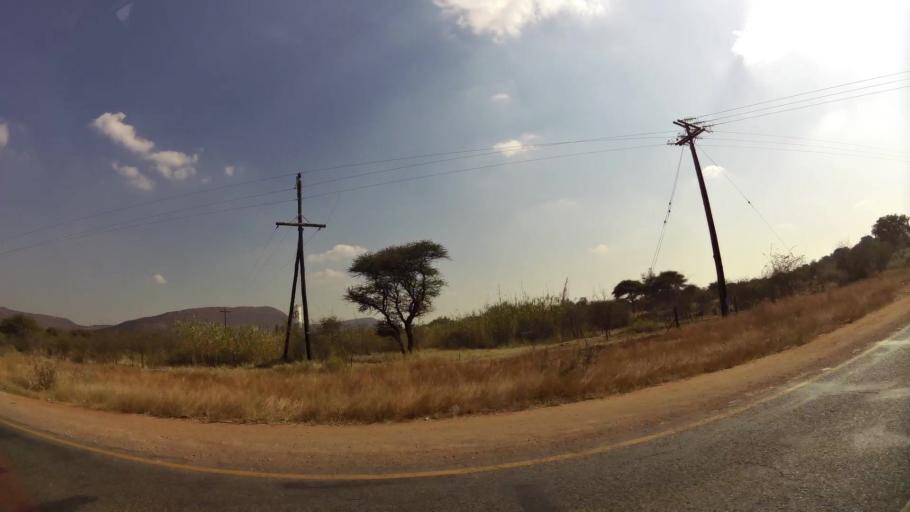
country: ZA
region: North-West
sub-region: Bojanala Platinum District Municipality
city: Mogwase
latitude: -25.4790
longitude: 27.0865
